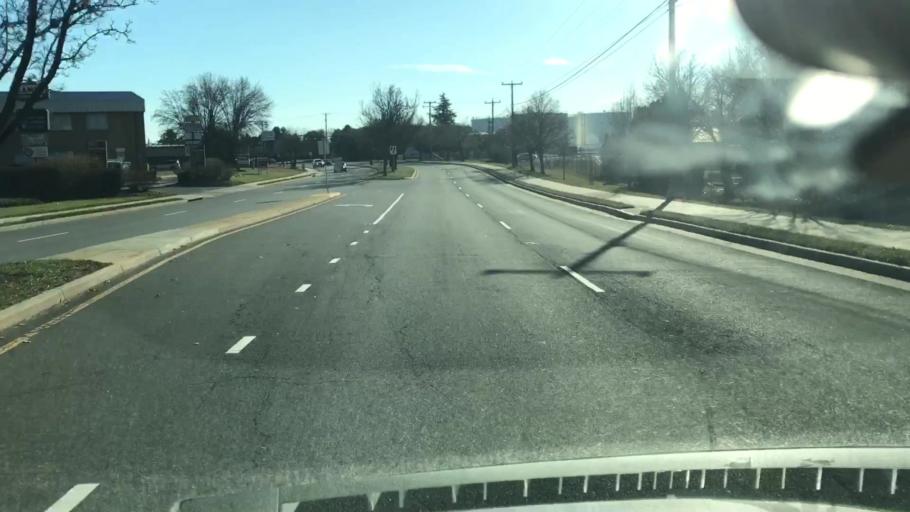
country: US
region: Virginia
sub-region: Fairfax County
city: Mantua
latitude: 38.8502
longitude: -77.2727
